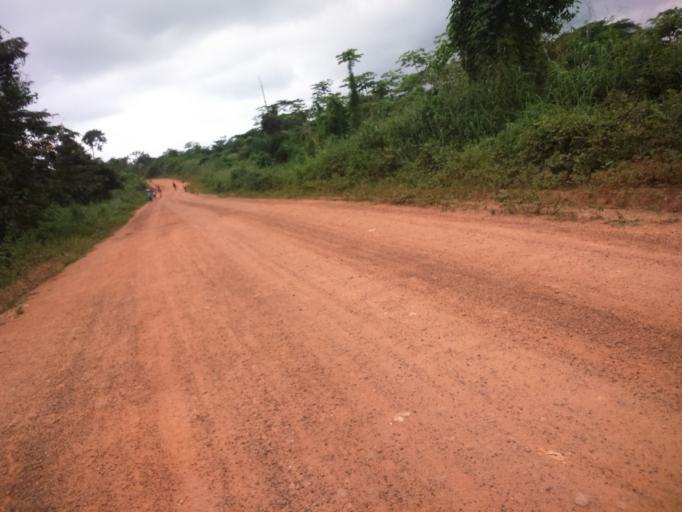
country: CI
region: Lagunes
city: Agou
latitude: 6.0764
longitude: -4.0682
